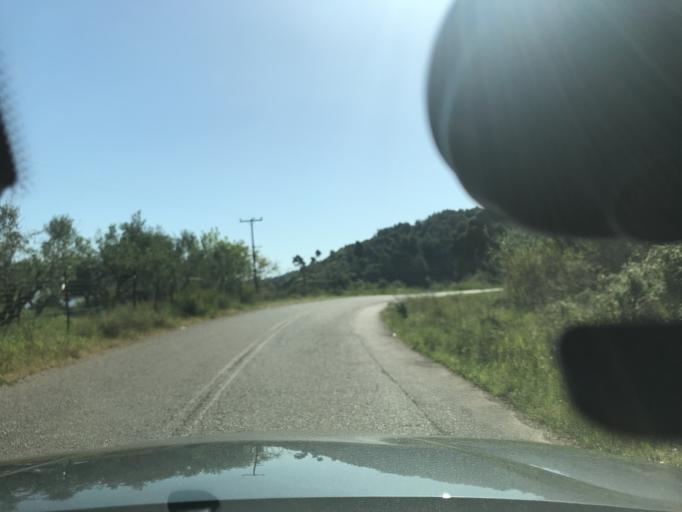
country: GR
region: West Greece
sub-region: Nomos Ileias
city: Epitalion
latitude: 37.6413
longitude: 21.5141
